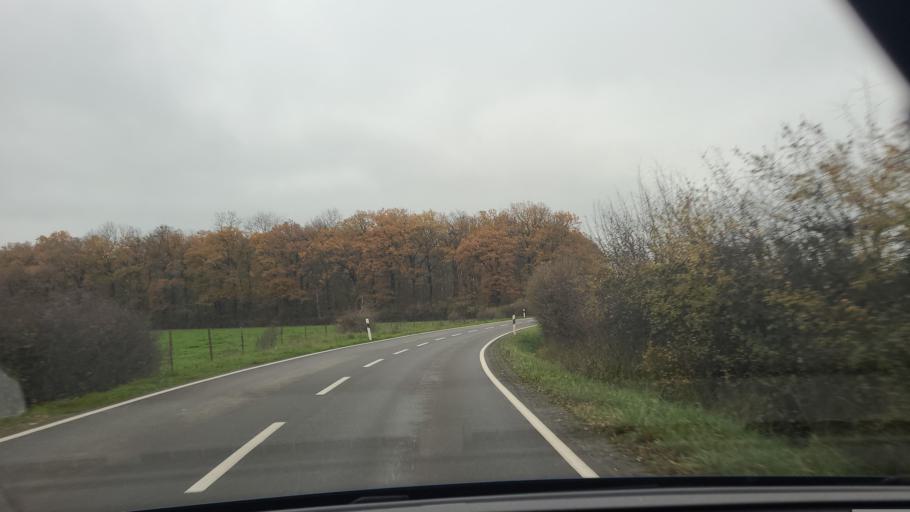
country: LU
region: Luxembourg
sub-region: Canton d'Esch-sur-Alzette
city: Mondercange
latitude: 49.5475
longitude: 5.9628
